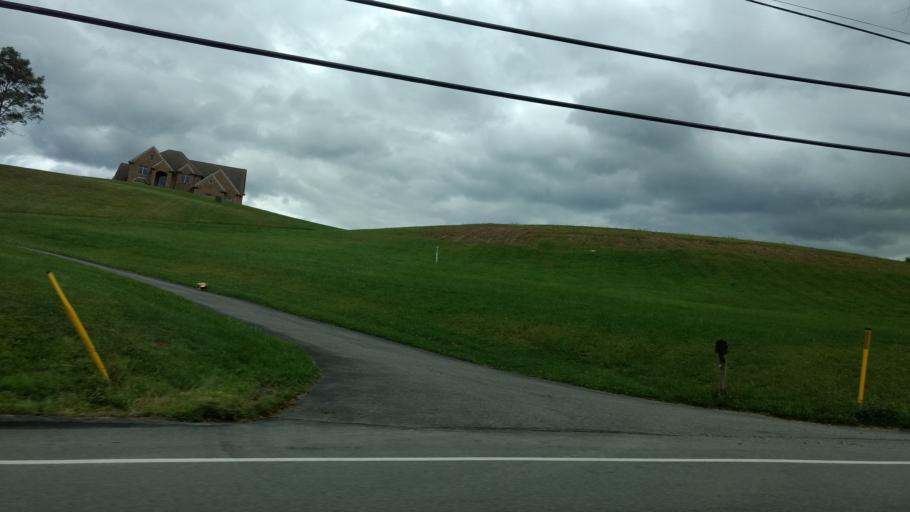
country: US
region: Pennsylvania
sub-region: Westmoreland County
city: Fellsburg
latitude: 40.1647
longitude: -79.8186
